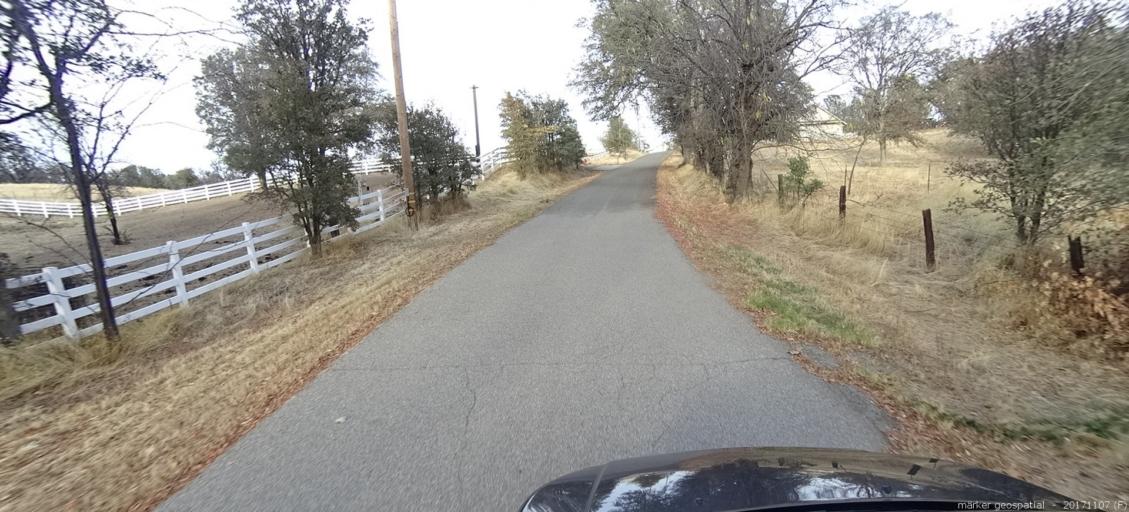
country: US
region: California
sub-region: Shasta County
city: Shasta
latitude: 40.5236
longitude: -122.4781
